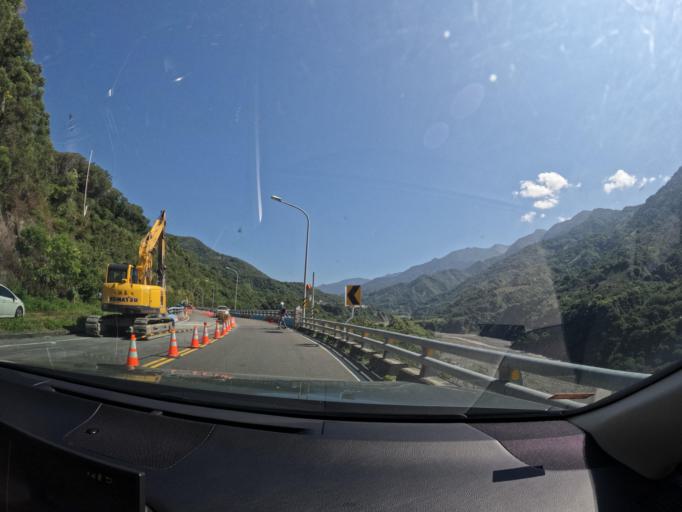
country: TW
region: Taiwan
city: Yujing
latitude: 23.1492
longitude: 120.7563
